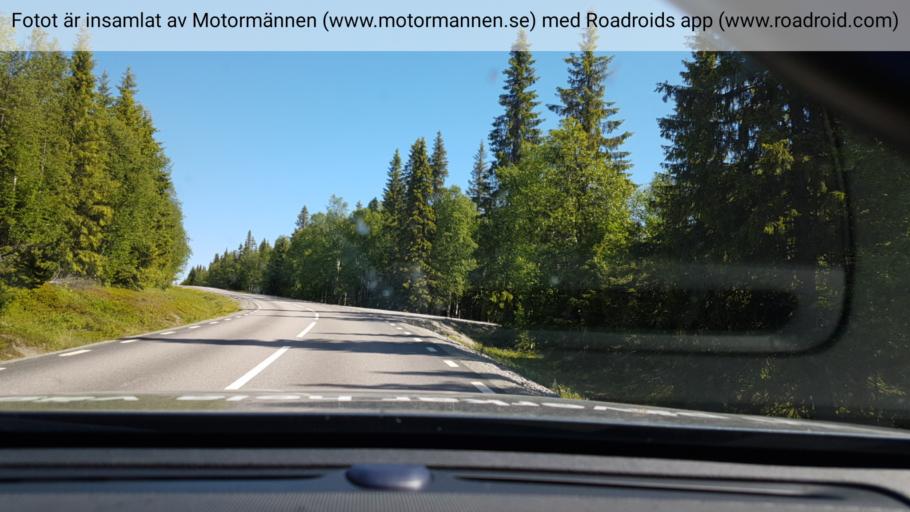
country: SE
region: Vaesterbotten
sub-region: Asele Kommun
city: Insjon
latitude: 64.7312
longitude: 17.4621
